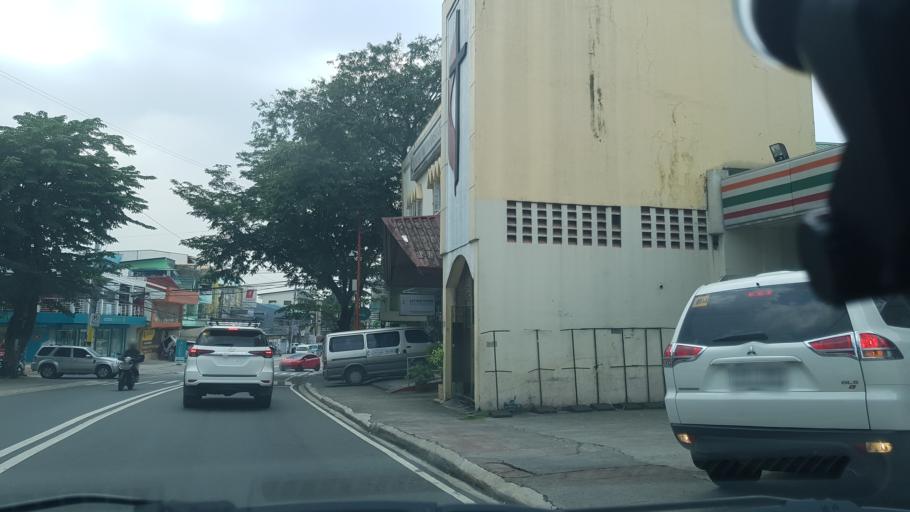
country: PH
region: Calabarzon
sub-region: Province of Rizal
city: Antipolo
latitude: 14.6425
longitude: 121.1220
